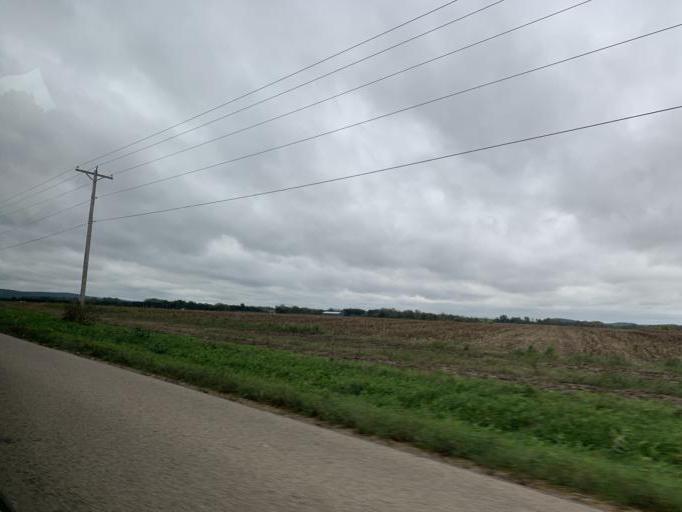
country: US
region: Wisconsin
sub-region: Sauk County
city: Prairie du Sac
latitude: 43.3339
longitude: -89.7695
